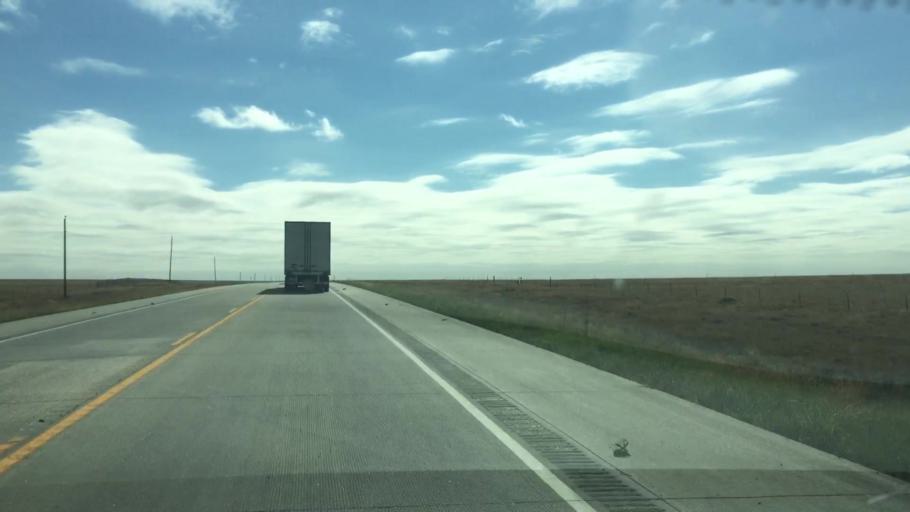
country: US
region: Colorado
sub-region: Lincoln County
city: Hugo
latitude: 39.0244
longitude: -103.3162
